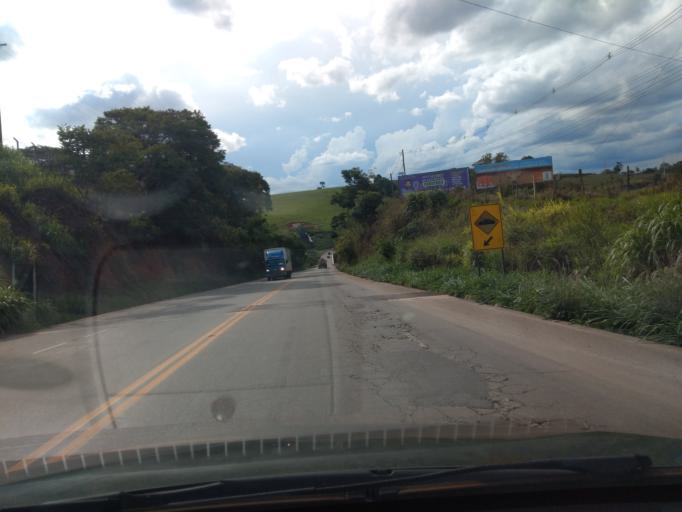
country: BR
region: Minas Gerais
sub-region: Varginha
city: Varginha
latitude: -21.6131
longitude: -45.4272
